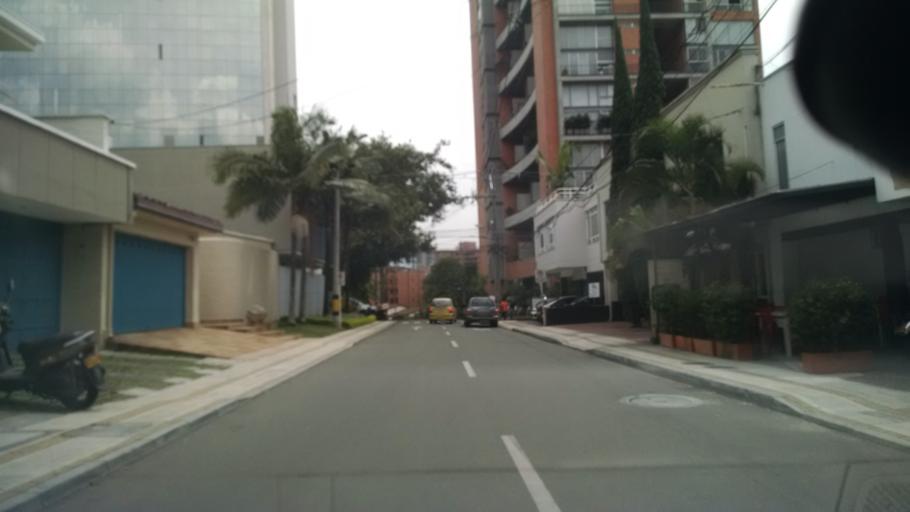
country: CO
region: Antioquia
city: Itagui
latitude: 6.2093
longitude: -75.5727
